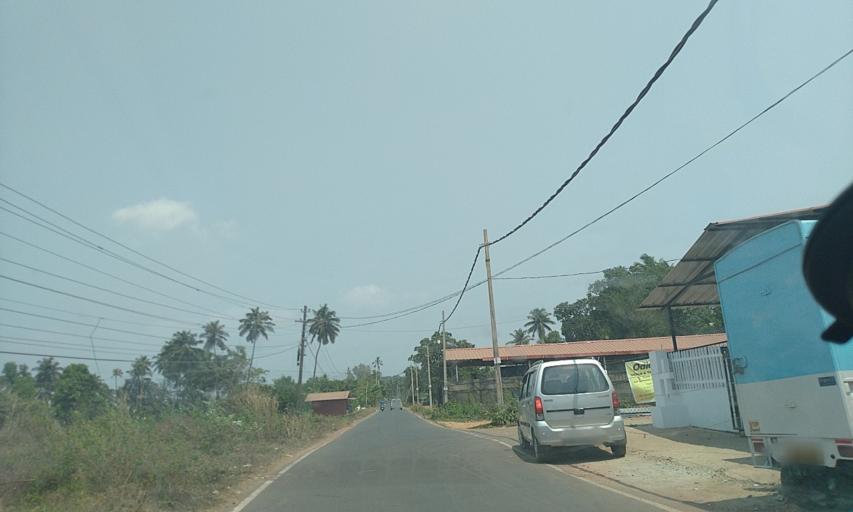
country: IN
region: Goa
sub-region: North Goa
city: Saligao
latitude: 15.5530
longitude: 73.8073
